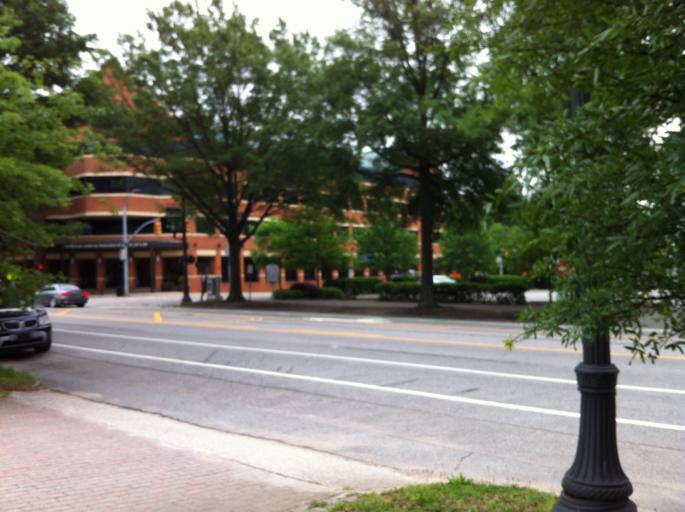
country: US
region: North Carolina
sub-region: Wake County
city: Raleigh
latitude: 35.7807
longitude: -78.6438
